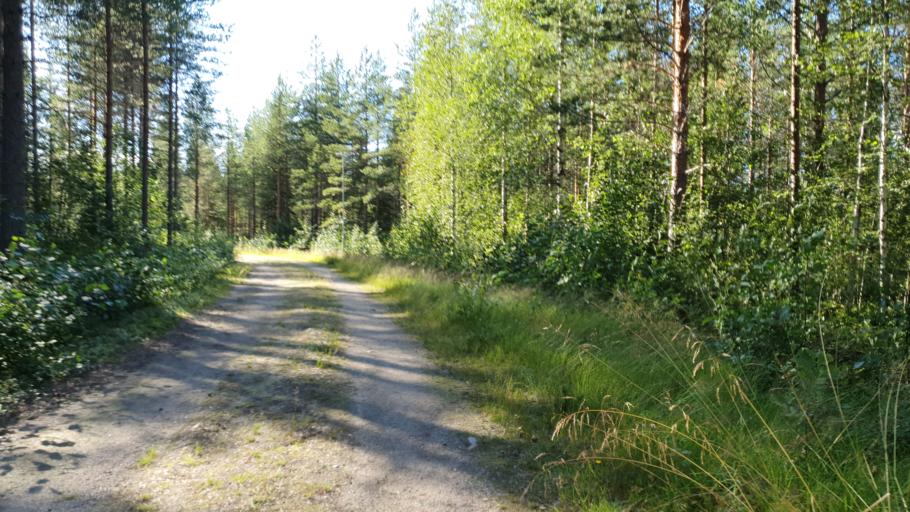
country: FI
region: Kainuu
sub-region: Kehys-Kainuu
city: Kuhmo
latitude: 64.1138
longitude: 29.5018
